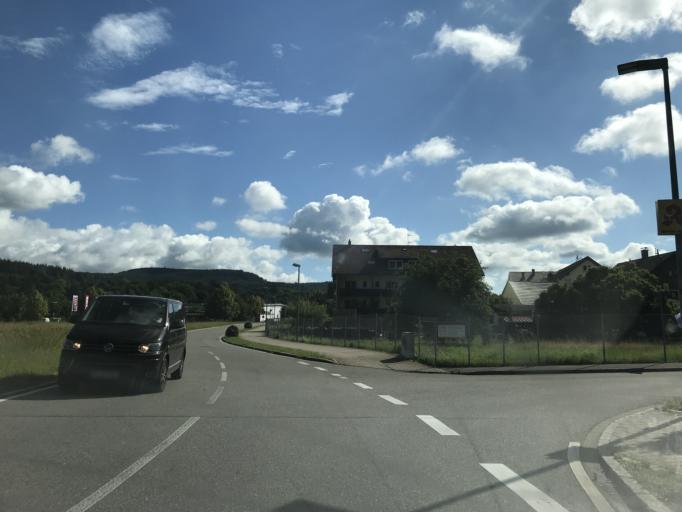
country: DE
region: Baden-Wuerttemberg
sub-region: Freiburg Region
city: Steinen
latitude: 47.6392
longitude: 7.7441
